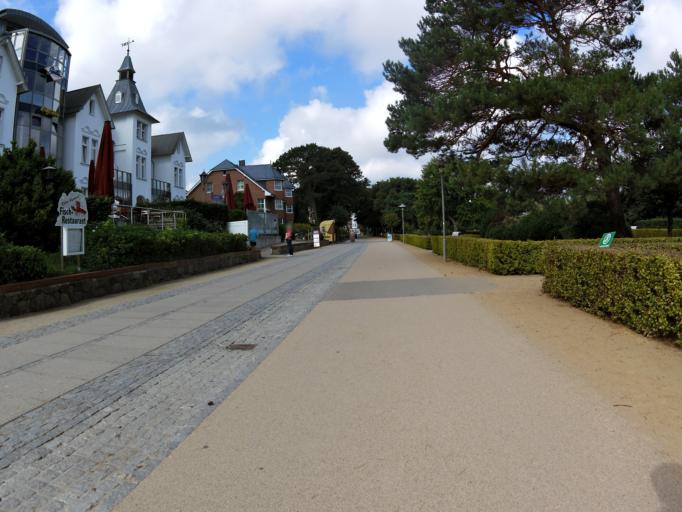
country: DE
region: Mecklenburg-Vorpommern
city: Ostseebad Zinnowitz
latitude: 54.0797
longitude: 13.9197
